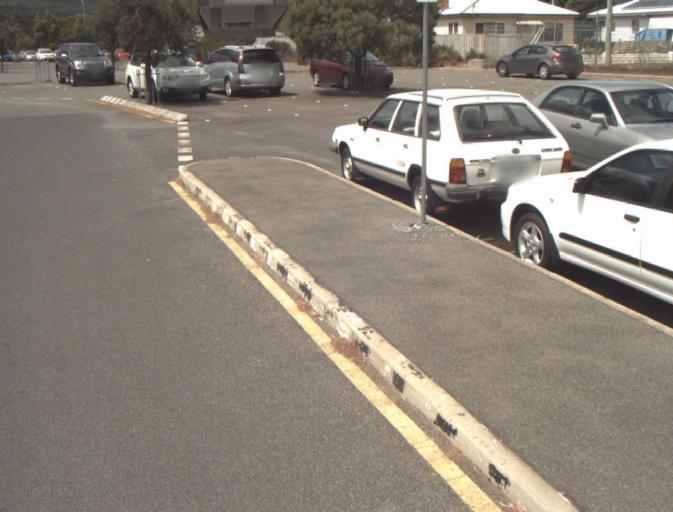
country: AU
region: Tasmania
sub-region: Launceston
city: Newnham
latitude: -41.4032
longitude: 147.1235
